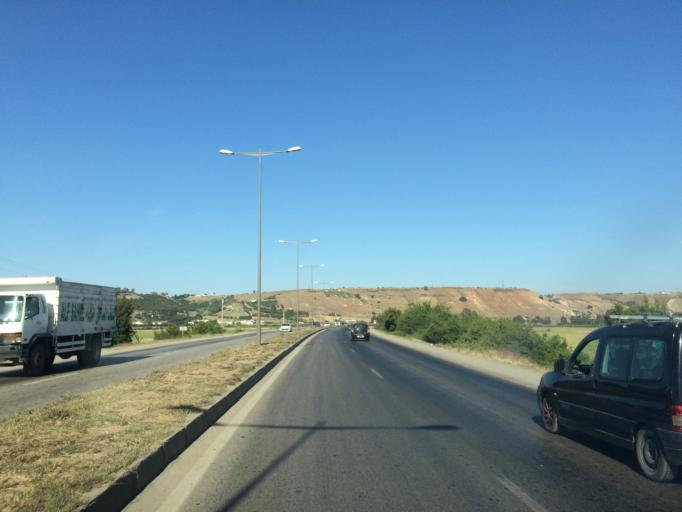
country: MA
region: Rabat-Sale-Zemmour-Zaer
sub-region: Rabat
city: Rabat
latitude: 33.9891
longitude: -6.7768
